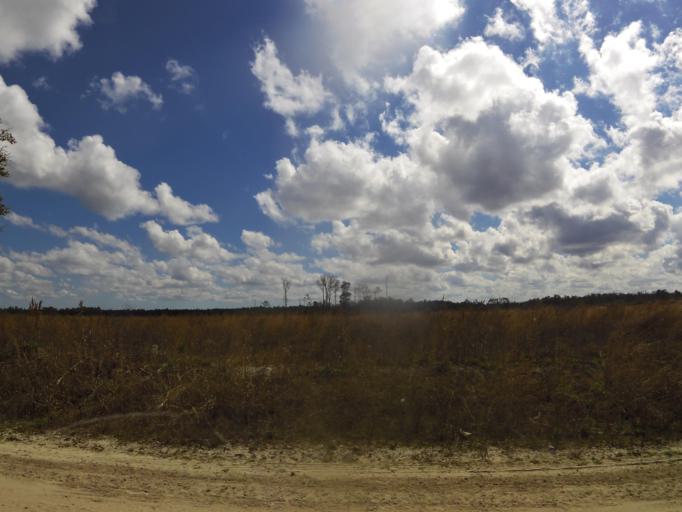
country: US
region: Florida
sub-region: Clay County
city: Green Cove Springs
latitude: 29.8413
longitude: -81.7264
